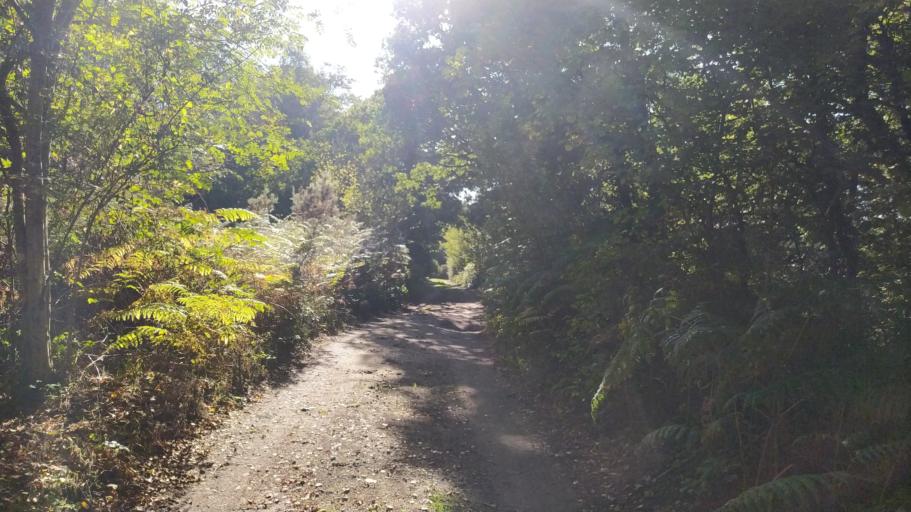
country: GB
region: England
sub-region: Hampshire
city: Kingsley
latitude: 51.1385
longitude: -0.8608
